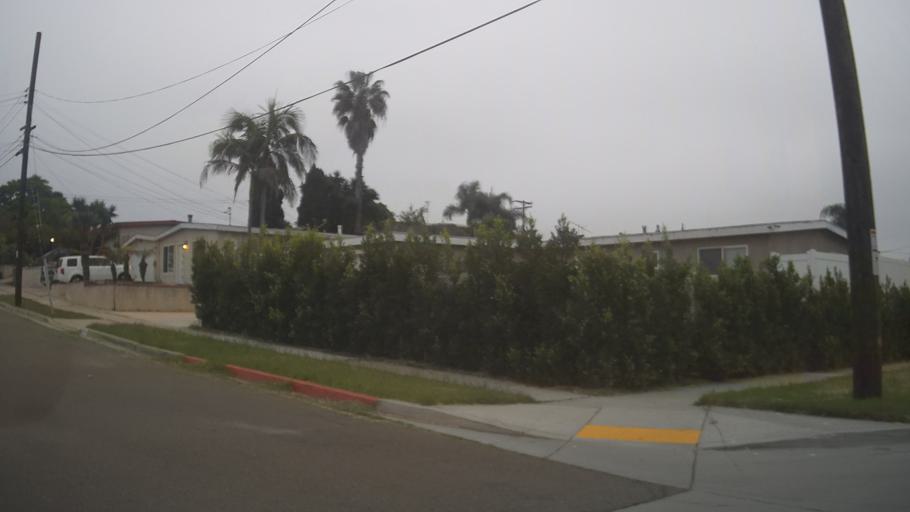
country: US
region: California
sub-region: San Diego County
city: Bonita
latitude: 32.6215
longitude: -117.0472
